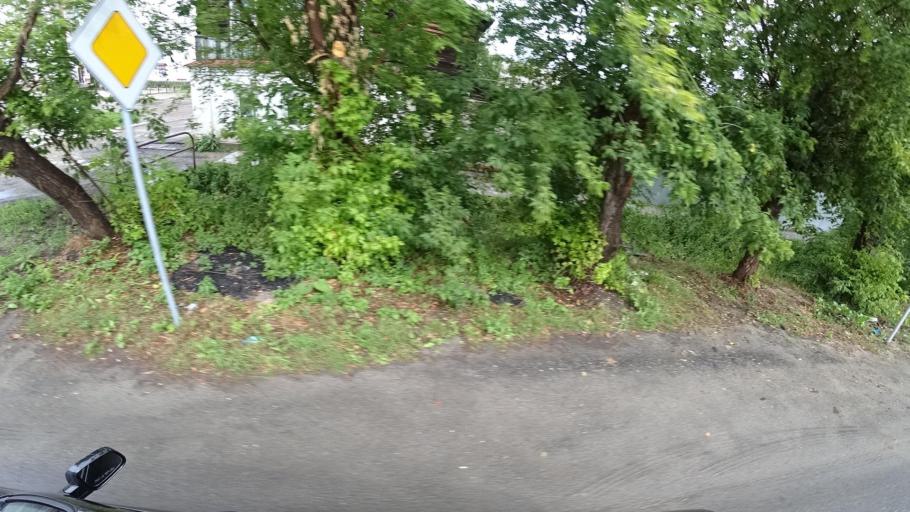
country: RU
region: Sverdlovsk
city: Kamyshlov
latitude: 56.8454
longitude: 62.7199
